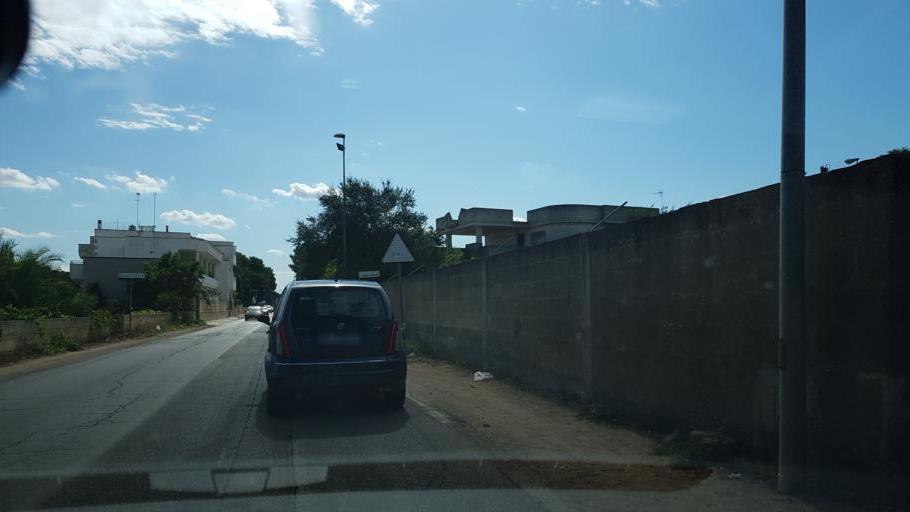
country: IT
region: Apulia
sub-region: Provincia di Lecce
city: Porto Cesareo
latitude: 40.2612
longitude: 17.9028
